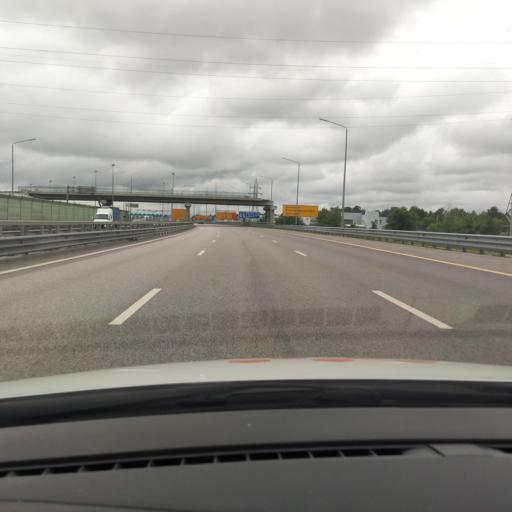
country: RU
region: Voronezj
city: Somovo
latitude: 51.6690
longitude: 39.3003
